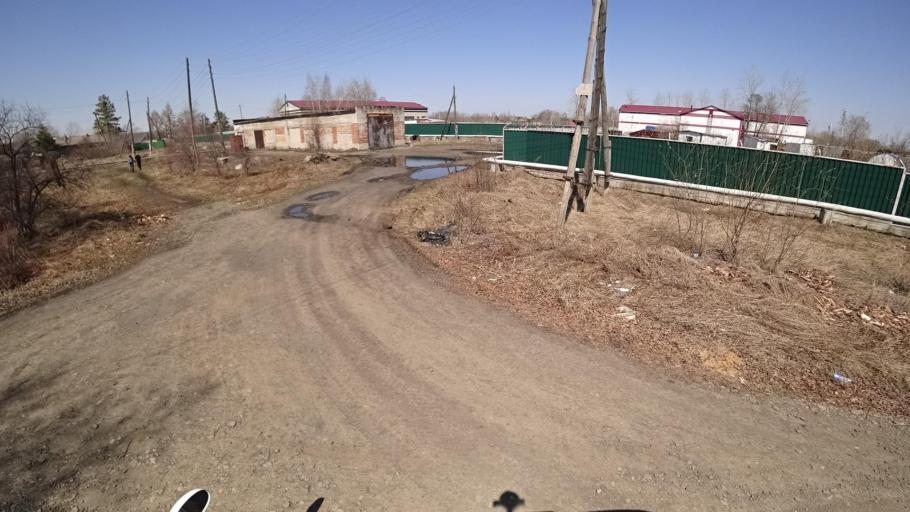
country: RU
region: Khabarovsk Krai
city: Khurba
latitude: 50.4073
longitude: 136.8887
